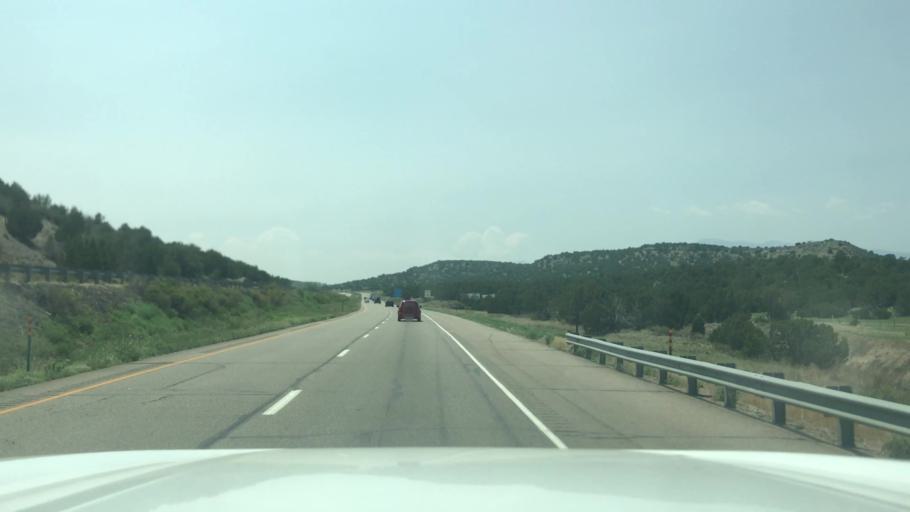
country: US
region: Colorado
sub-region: Pueblo County
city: Colorado City
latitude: 37.9899
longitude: -104.7679
